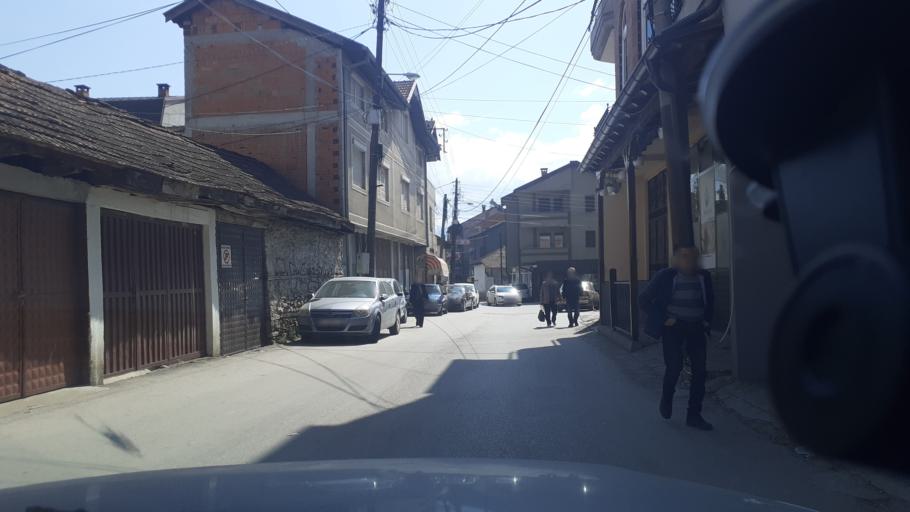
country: MK
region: Tetovo
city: Tetovo
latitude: 42.0043
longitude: 20.9673
